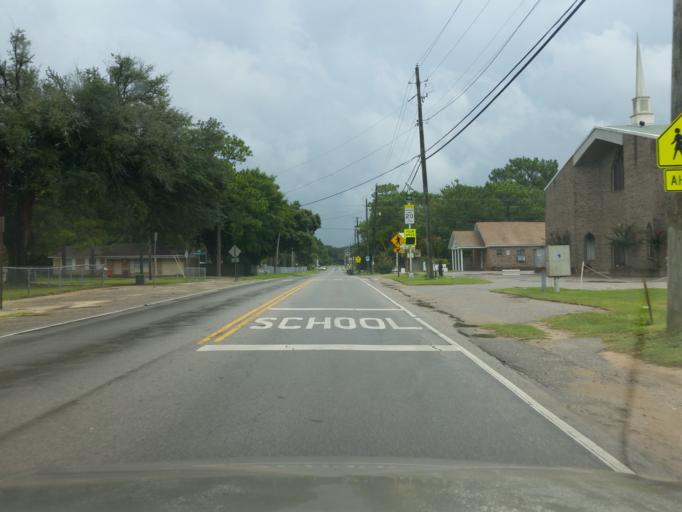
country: US
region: Florida
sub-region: Escambia County
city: Brent
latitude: 30.4528
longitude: -87.2605
